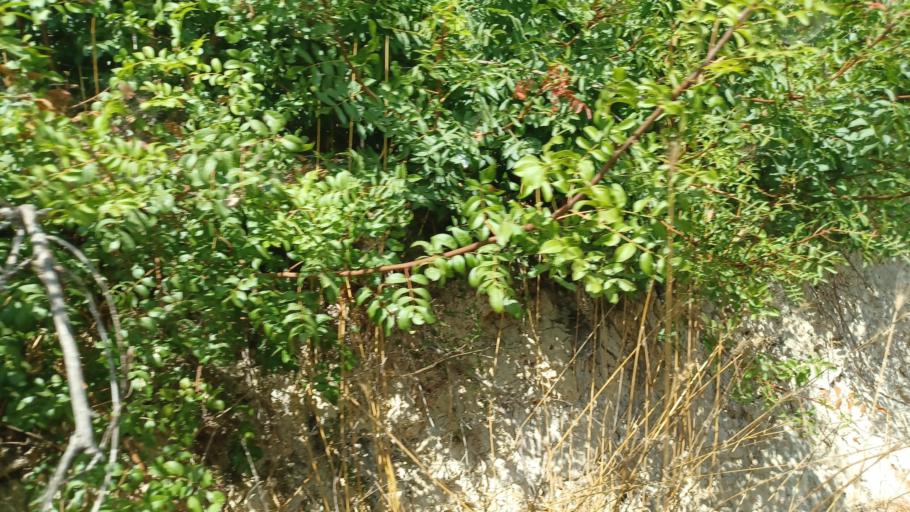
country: CY
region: Pafos
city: Tala
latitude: 34.8620
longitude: 32.4580
